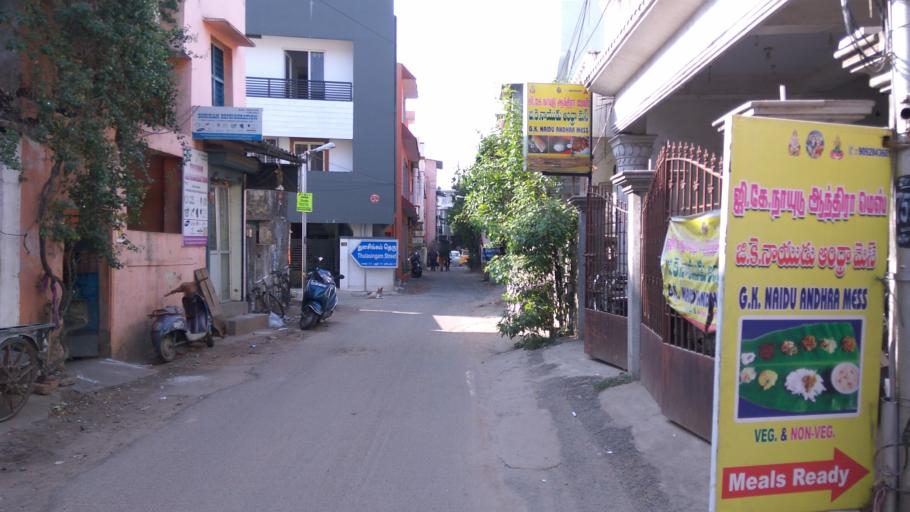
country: IN
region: Tamil Nadu
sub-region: Kancheepuram
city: Alandur
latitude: 13.0128
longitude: 80.2234
